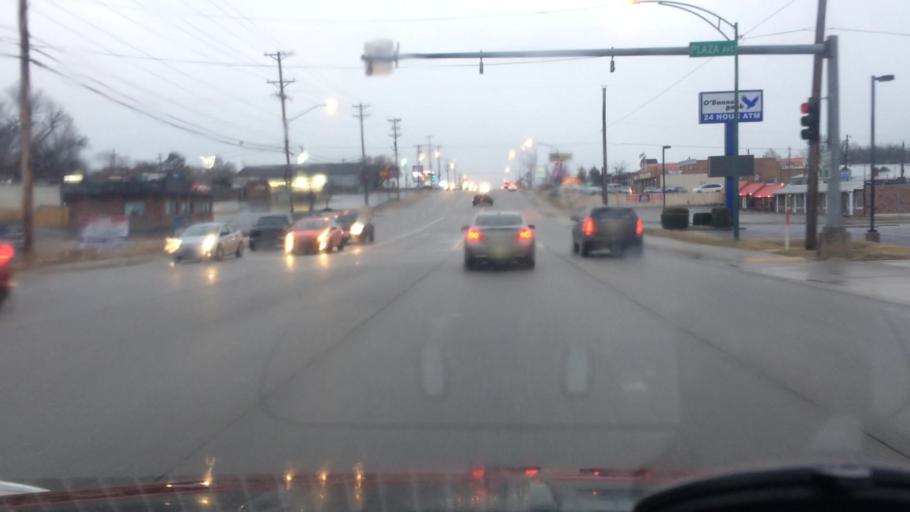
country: US
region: Missouri
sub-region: Greene County
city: Springfield
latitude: 37.1805
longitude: -93.2335
